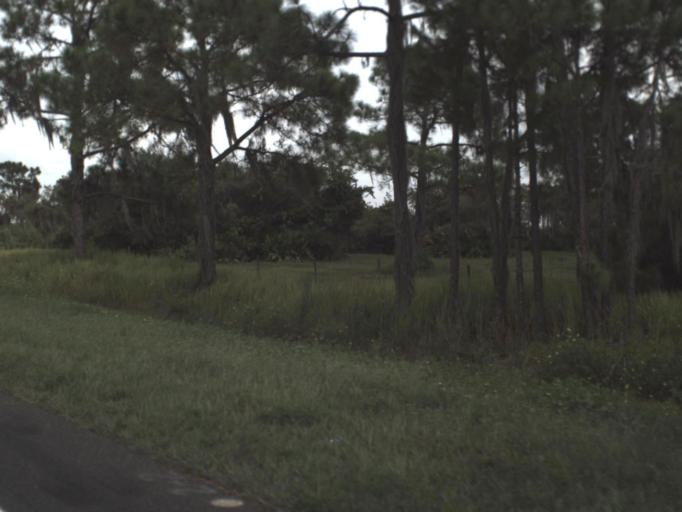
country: US
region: Florida
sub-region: Polk County
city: Crooked Lake Park
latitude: 27.7850
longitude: -81.5971
